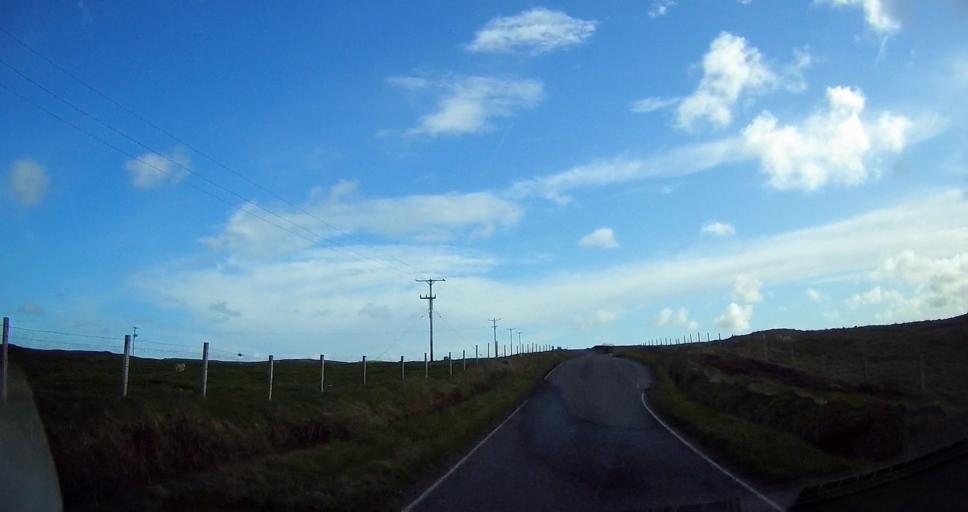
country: GB
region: Scotland
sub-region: Shetland Islands
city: Shetland
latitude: 60.3645
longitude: -1.1418
